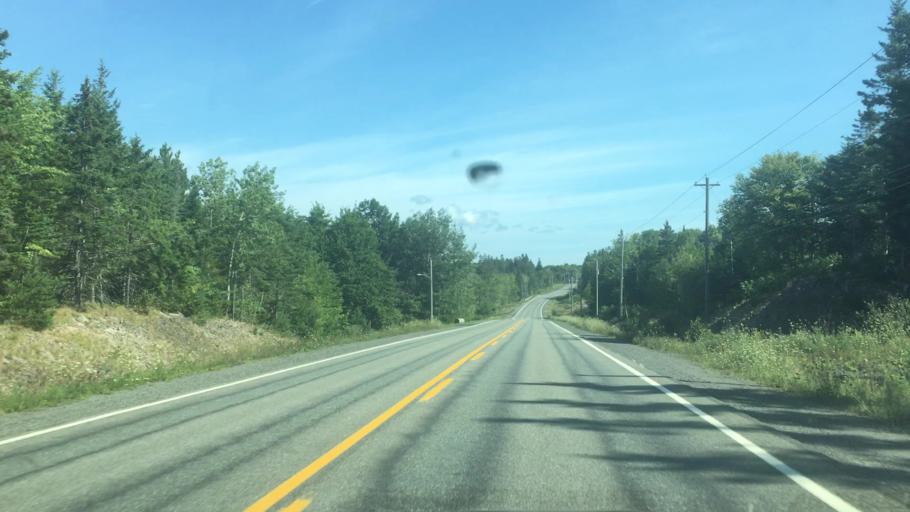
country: CA
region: Nova Scotia
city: Sydney
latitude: 45.9909
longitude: -60.4122
